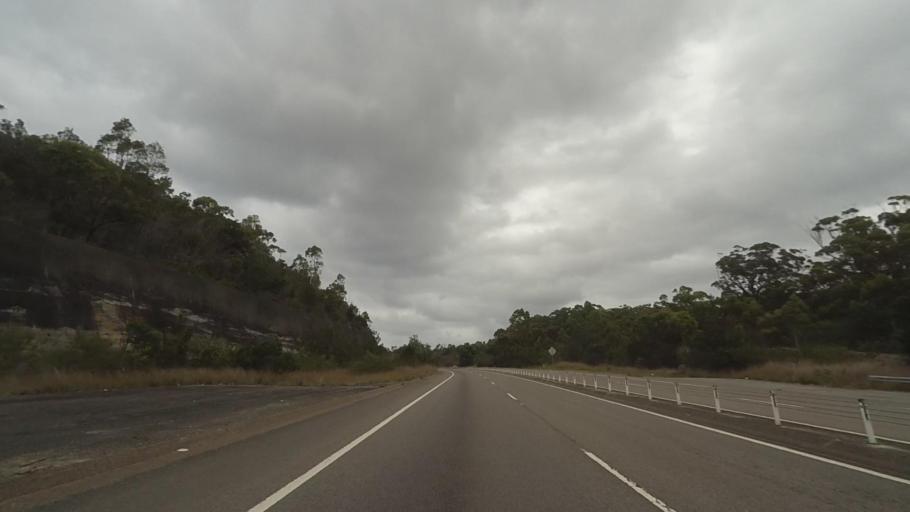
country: AU
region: New South Wales
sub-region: Lake Macquarie Shire
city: Arcadia vale
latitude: -33.1174
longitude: 151.6288
